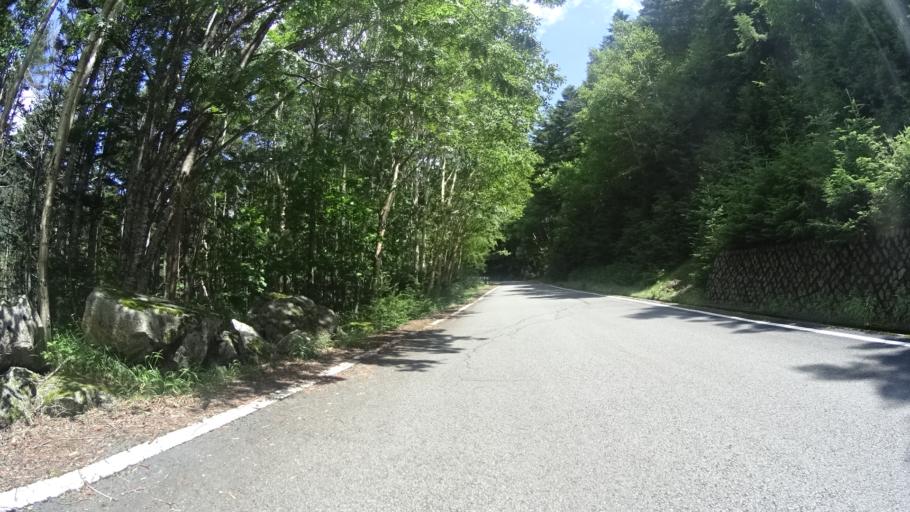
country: JP
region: Yamanashi
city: Enzan
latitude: 35.8613
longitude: 138.6497
